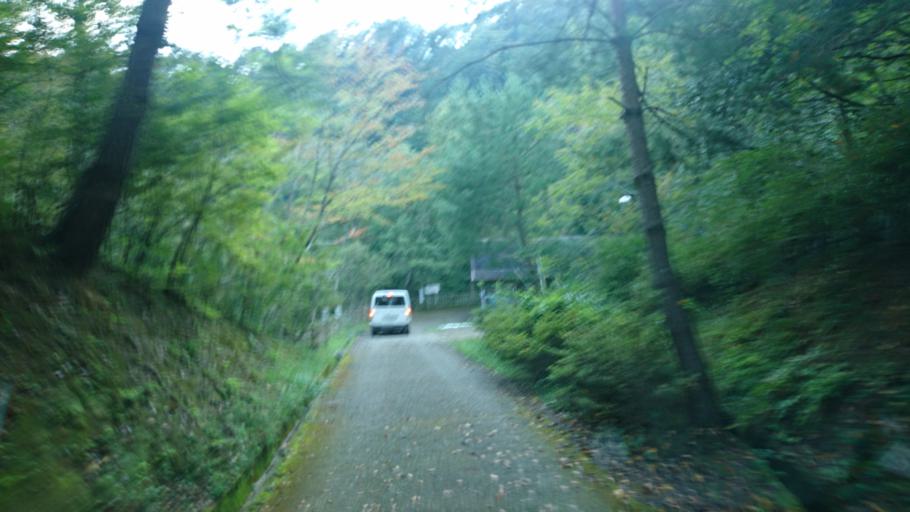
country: JP
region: Chiba
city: Kawaguchi
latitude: 35.1746
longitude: 140.0164
